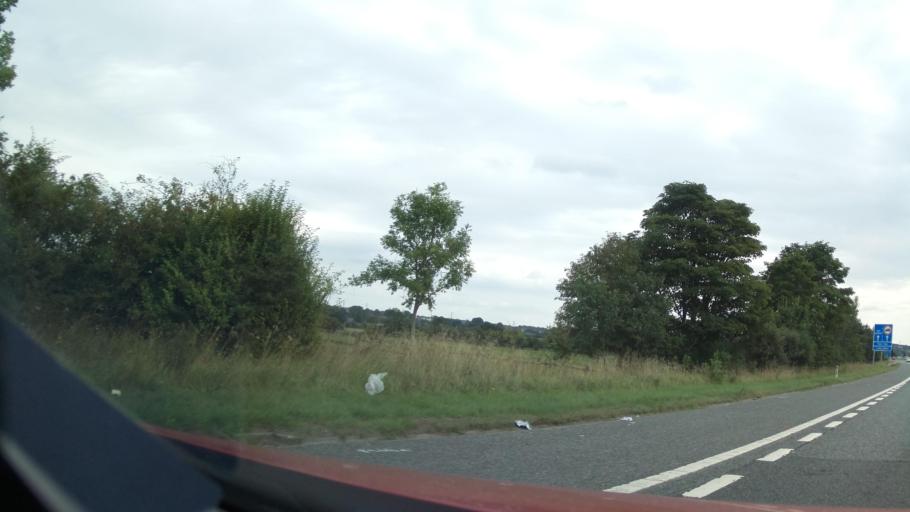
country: GB
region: England
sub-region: County Durham
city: Coxhoe
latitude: 54.7241
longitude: -1.5219
